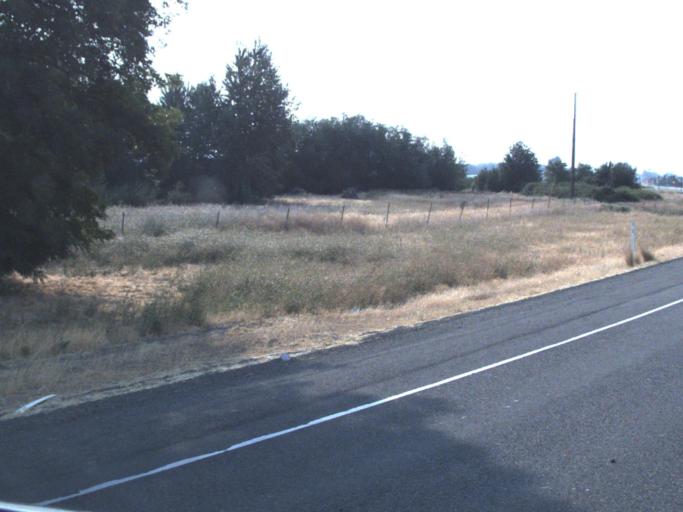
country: US
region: Washington
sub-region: Kittitas County
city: Ellensburg
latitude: 47.0125
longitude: -120.5938
